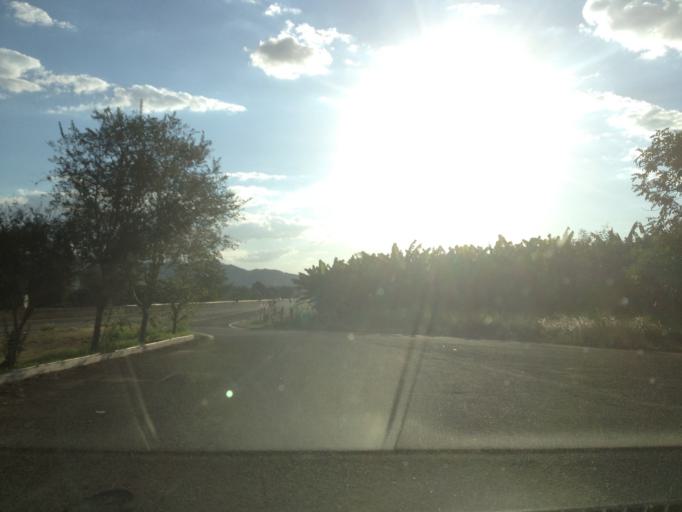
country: BR
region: Sao Paulo
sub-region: Brotas
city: Brotas
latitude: -22.2654
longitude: -48.2150
